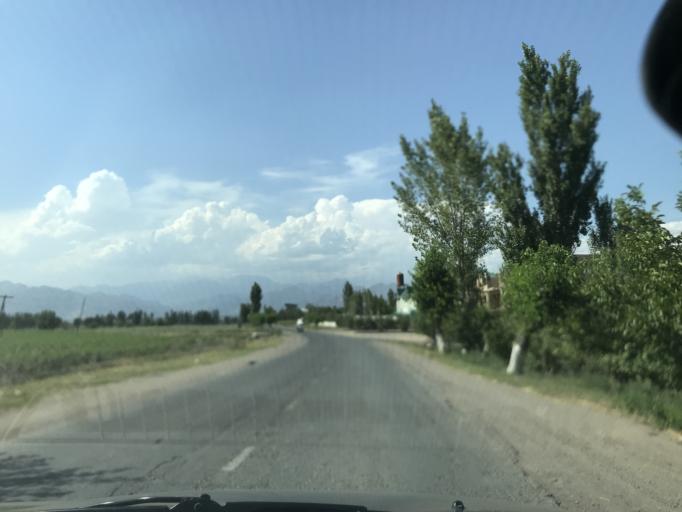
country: UZ
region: Namangan
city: Chust Shahri
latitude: 41.0244
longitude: 71.2187
